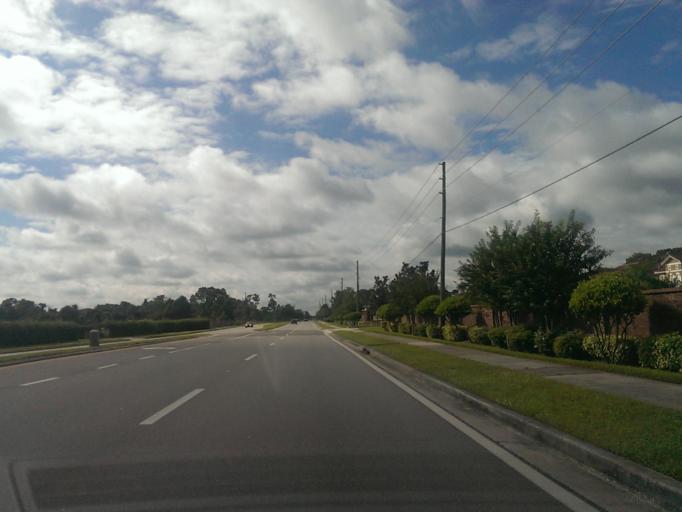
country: US
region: Florida
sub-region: Orange County
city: Doctor Phillips
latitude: 28.4196
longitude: -81.5328
